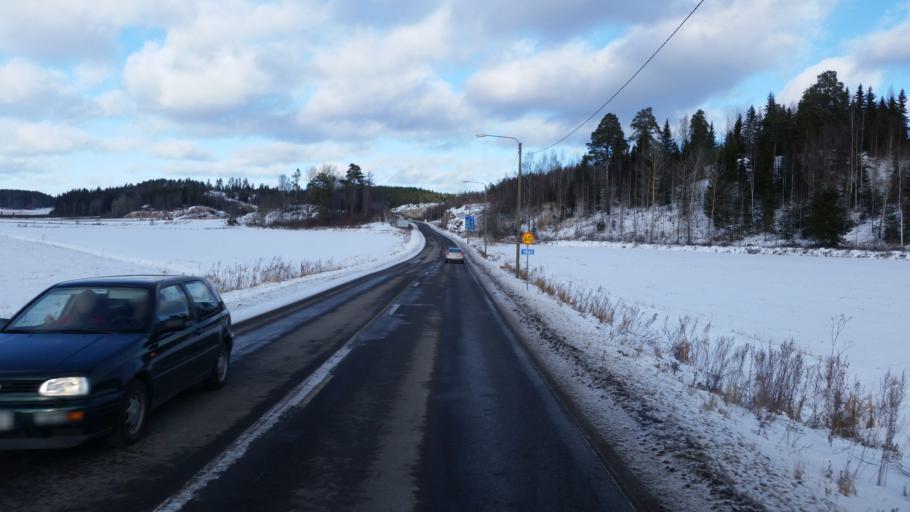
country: FI
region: Varsinais-Suomi
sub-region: Salo
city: Muurla
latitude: 60.3740
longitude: 23.3140
